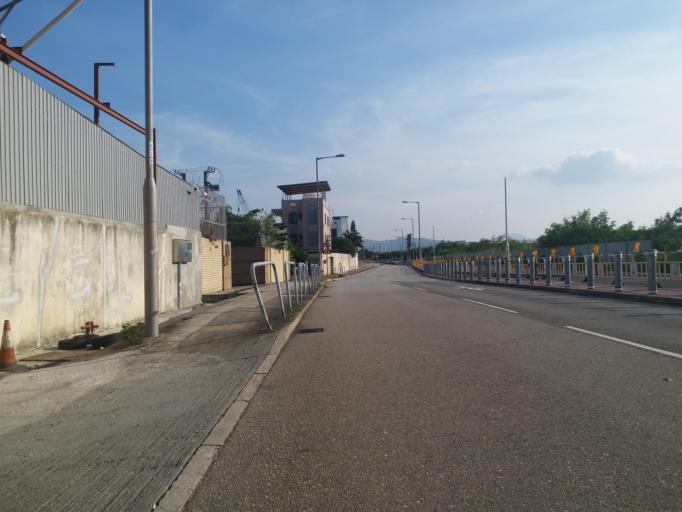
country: HK
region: Yuen Long
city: Yuen Long Kau Hui
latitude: 22.4725
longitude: 114.0509
